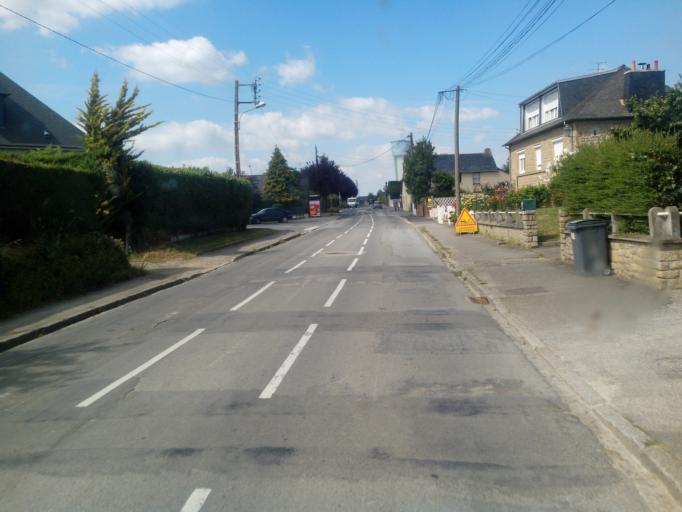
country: FR
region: Brittany
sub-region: Departement d'Ille-et-Vilaine
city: Acigne
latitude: 48.1361
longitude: -1.5334
